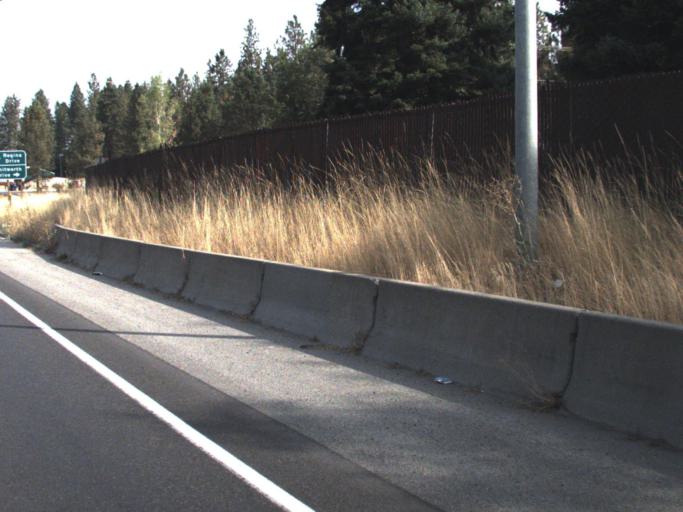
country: US
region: Washington
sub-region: Spokane County
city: Fairwood
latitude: 47.7617
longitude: -117.4072
